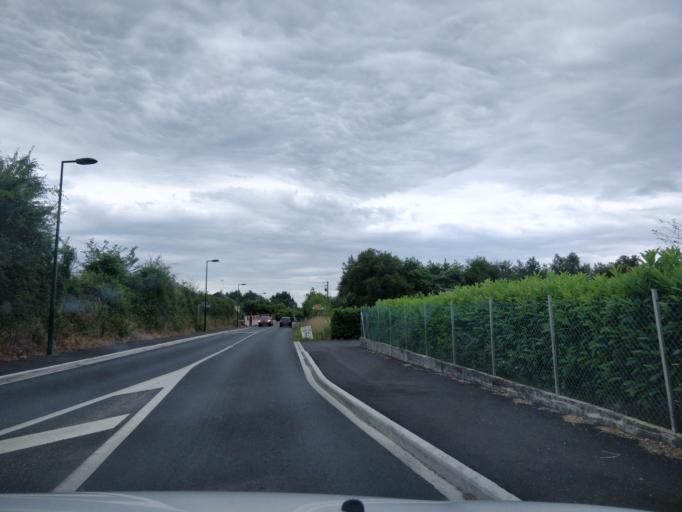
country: FR
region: Pays de la Loire
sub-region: Departement de Maine-et-Loire
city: Feneu
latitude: 47.5674
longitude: -0.5879
